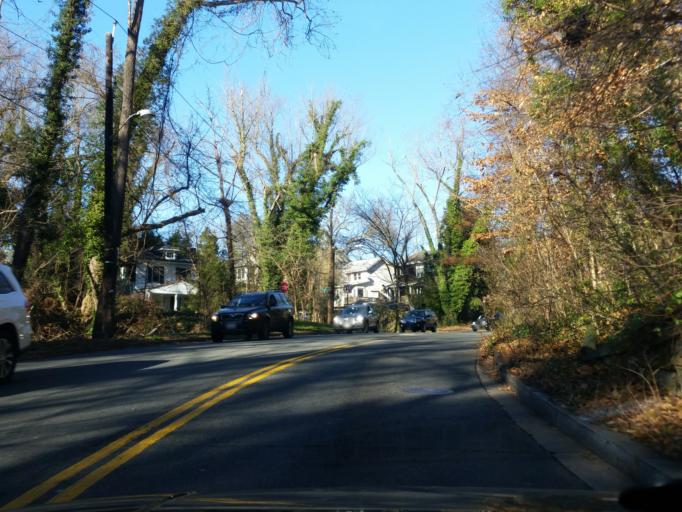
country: US
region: Maryland
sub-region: Montgomery County
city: Brookmont
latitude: 38.9258
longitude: -77.1068
